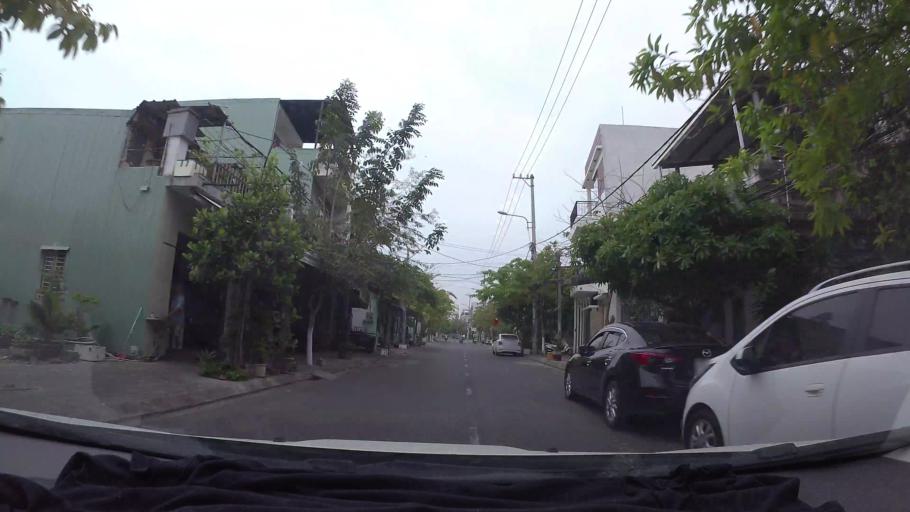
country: VN
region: Da Nang
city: Thanh Khe
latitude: 16.0567
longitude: 108.1745
